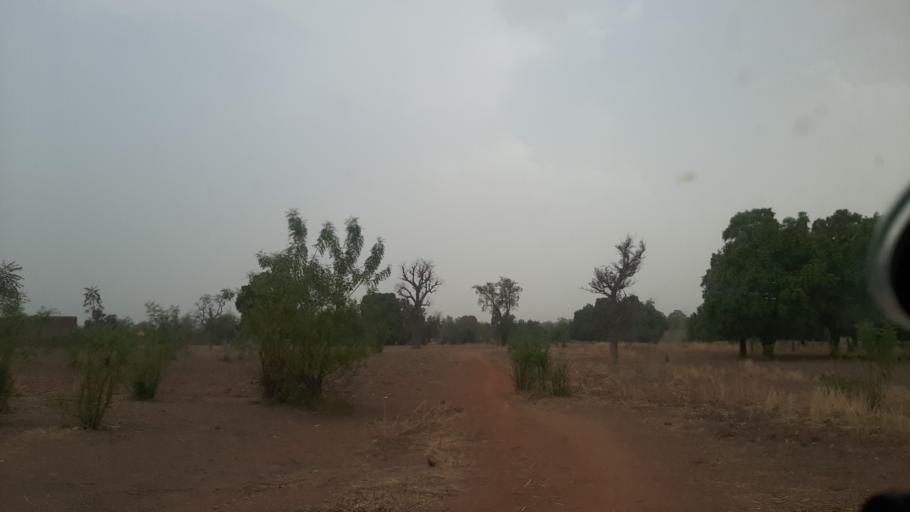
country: BF
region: Boucle du Mouhoun
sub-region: Province des Banwa
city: Salanso
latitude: 11.8706
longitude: -4.4490
